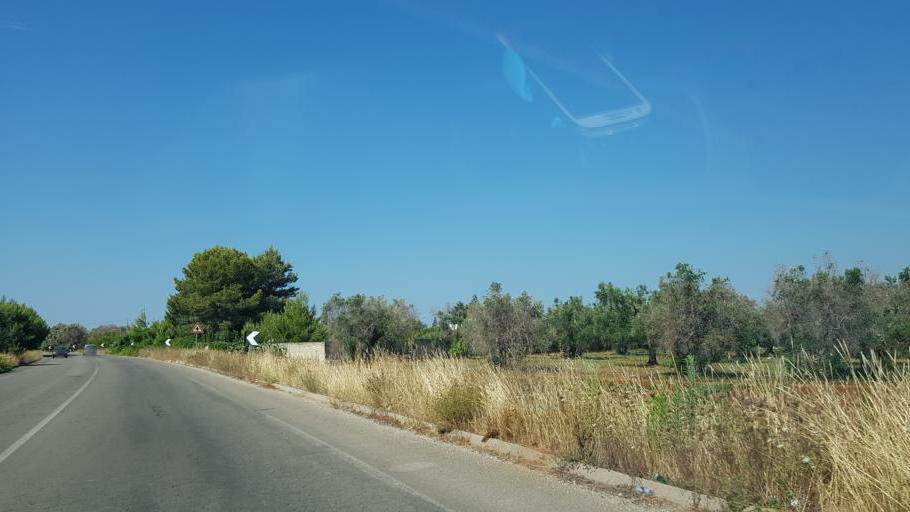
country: IT
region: Apulia
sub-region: Provincia di Lecce
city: Veglie
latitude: 40.3434
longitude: 17.9436
